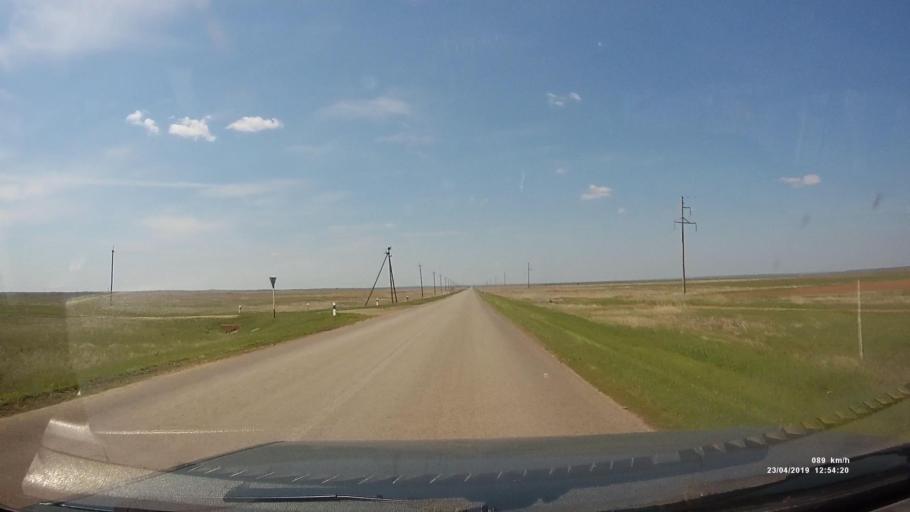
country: RU
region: Kalmykiya
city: Yashalta
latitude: 46.5795
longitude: 42.5802
